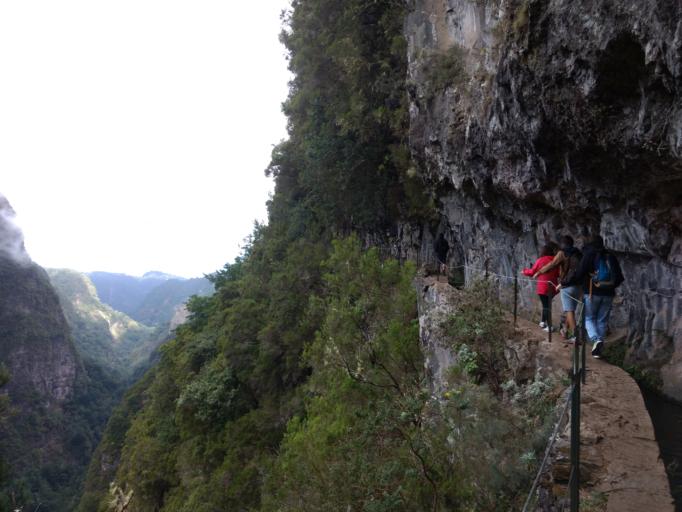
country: PT
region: Madeira
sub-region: Santana
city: Santana
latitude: 32.7764
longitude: -16.9360
